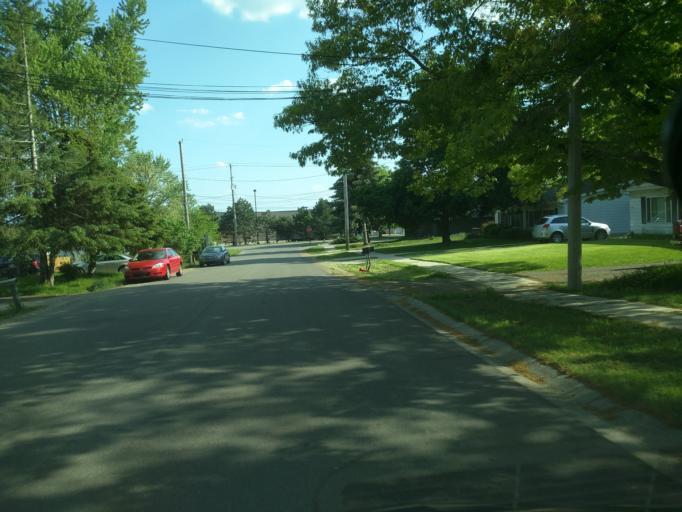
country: US
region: Michigan
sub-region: Eaton County
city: Waverly
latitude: 42.7275
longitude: -84.6055
